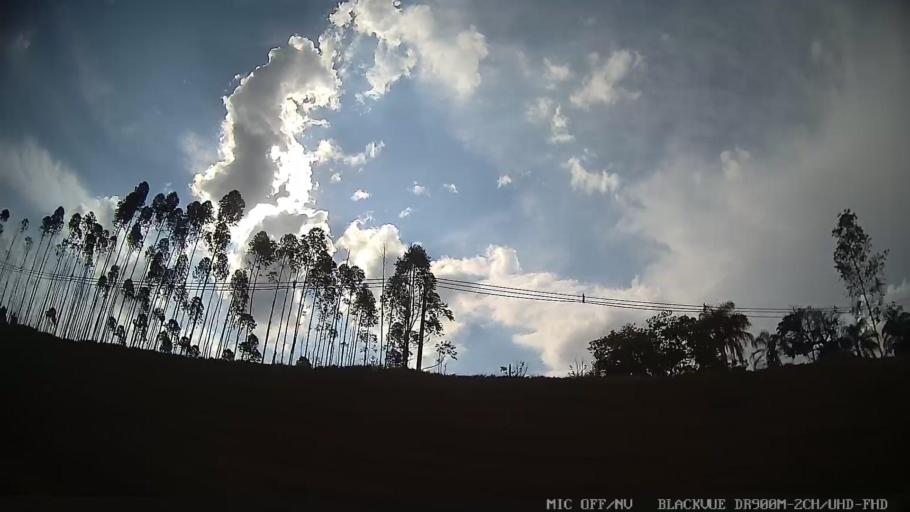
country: BR
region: Sao Paulo
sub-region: Braganca Paulista
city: Braganca Paulista
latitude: -22.9068
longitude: -46.5450
